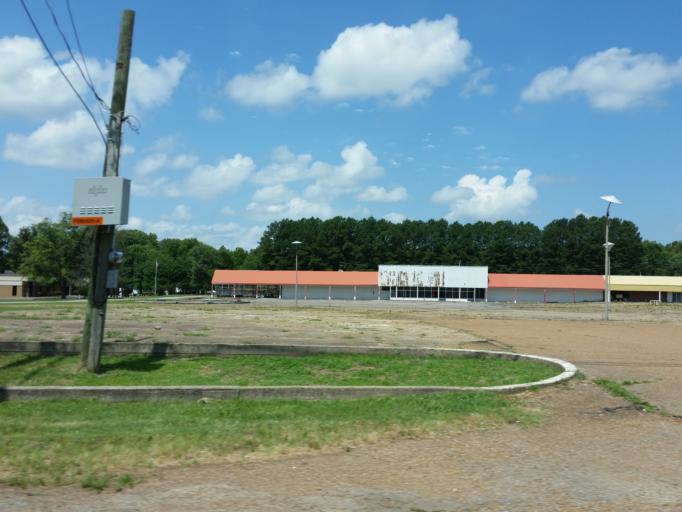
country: US
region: Tennessee
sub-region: Weakley County
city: Martin
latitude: 36.3658
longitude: -88.8502
